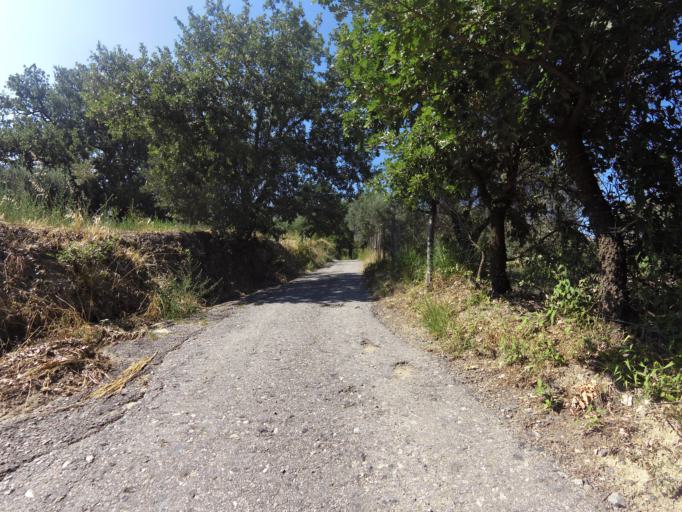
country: IT
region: Calabria
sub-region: Provincia di Reggio Calabria
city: Pazzano
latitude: 38.4588
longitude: 16.4586
